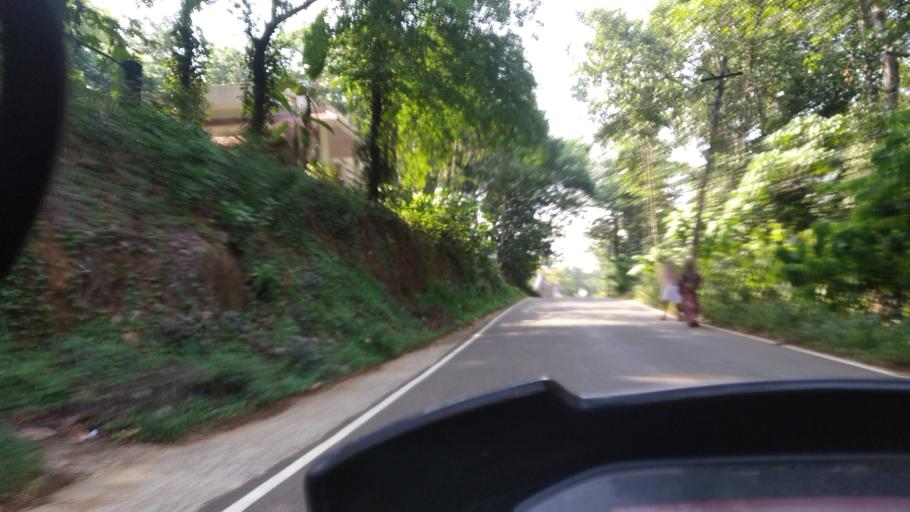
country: IN
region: Kerala
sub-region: Ernakulam
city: Piravam
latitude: 9.8232
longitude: 76.5498
